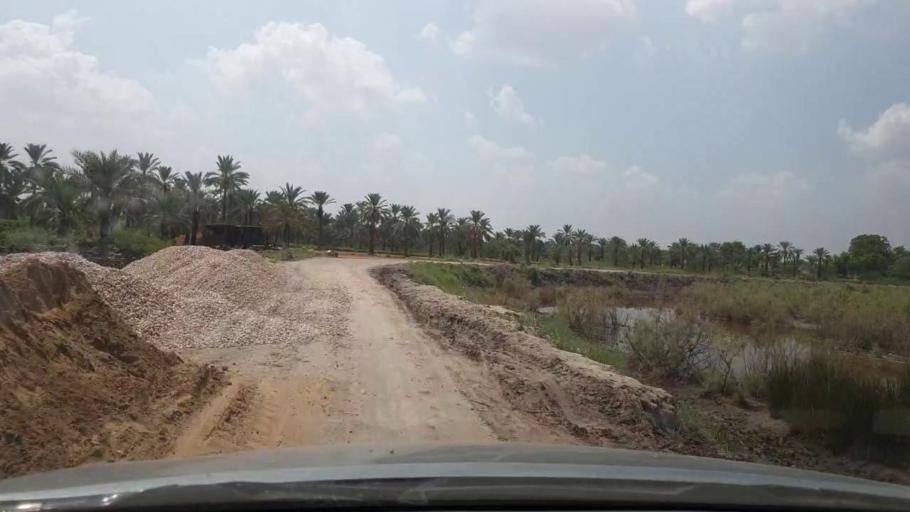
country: PK
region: Sindh
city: Kot Diji
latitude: 27.3984
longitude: 68.7387
